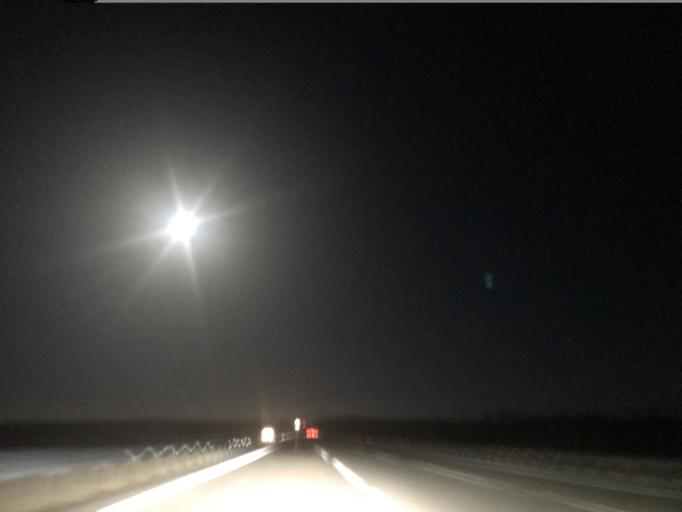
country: TR
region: Nigde
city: Ulukisla
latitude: 37.6389
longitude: 34.3913
